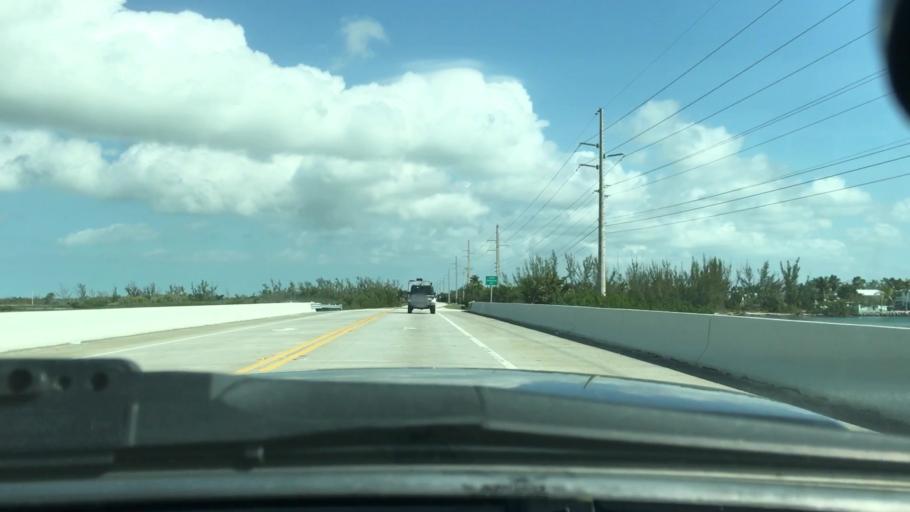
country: US
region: Florida
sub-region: Monroe County
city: Cudjoe Key
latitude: 24.6412
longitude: -81.5734
